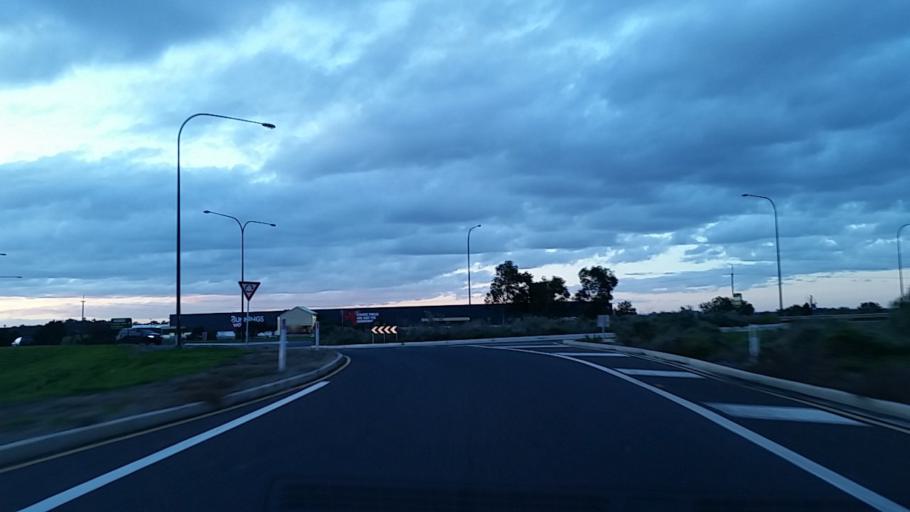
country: AU
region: South Australia
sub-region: Playford
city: Angle Vale
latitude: -34.6625
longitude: 138.6531
